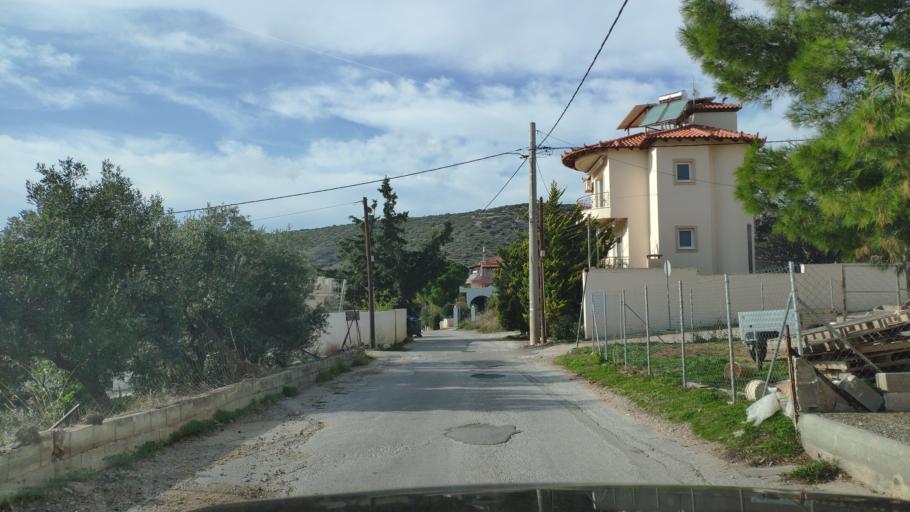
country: GR
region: Attica
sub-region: Nomarchia Anatolikis Attikis
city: Limin Mesoyaias
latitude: 37.8999
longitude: 24.0257
